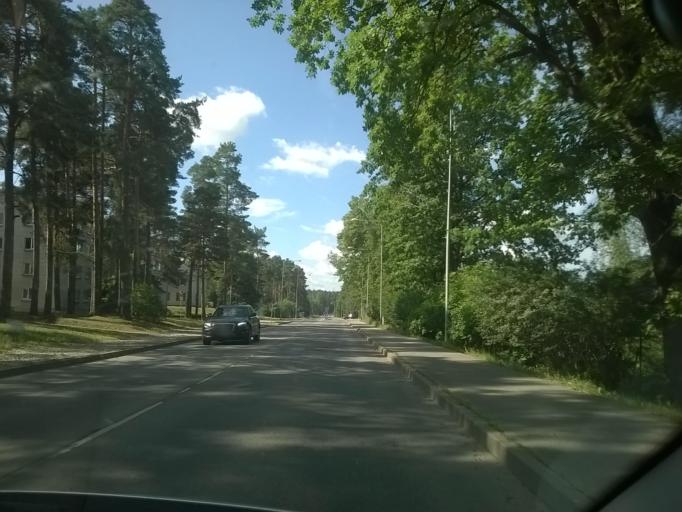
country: EE
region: Vorumaa
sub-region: Voru linn
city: Voru
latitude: 57.8245
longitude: 27.0045
